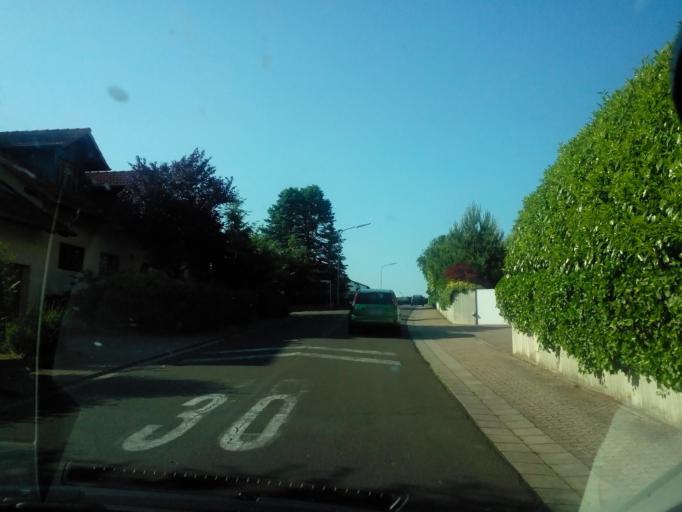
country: DE
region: Saarland
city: Beckingen
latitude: 49.3881
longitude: 6.7067
